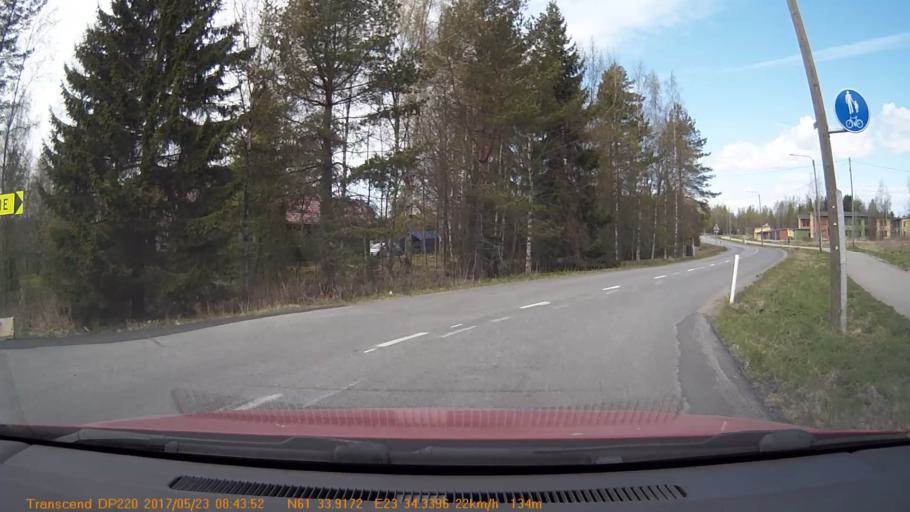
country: FI
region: Pirkanmaa
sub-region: Tampere
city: Yloejaervi
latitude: 61.5651
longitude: 23.5728
